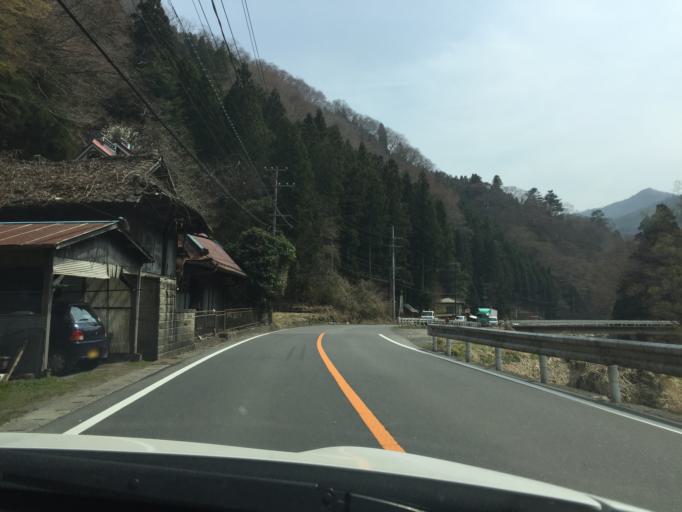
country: JP
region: Fukushima
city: Ishikawa
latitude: 37.0501
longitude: 140.6180
